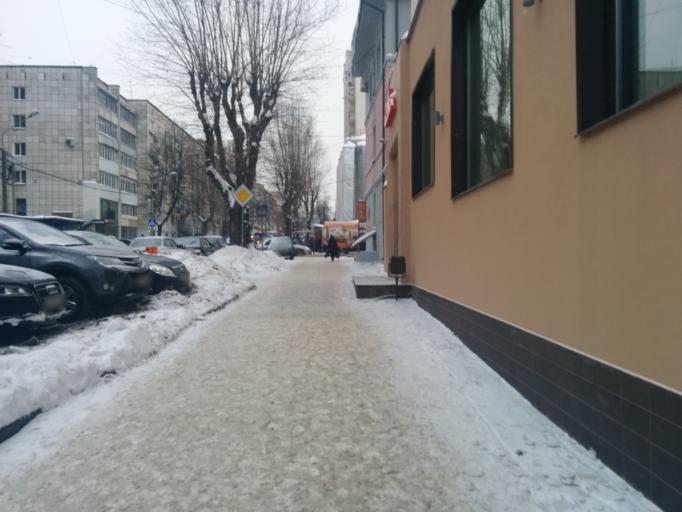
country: RU
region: Perm
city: Perm
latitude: 58.0136
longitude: 56.2497
